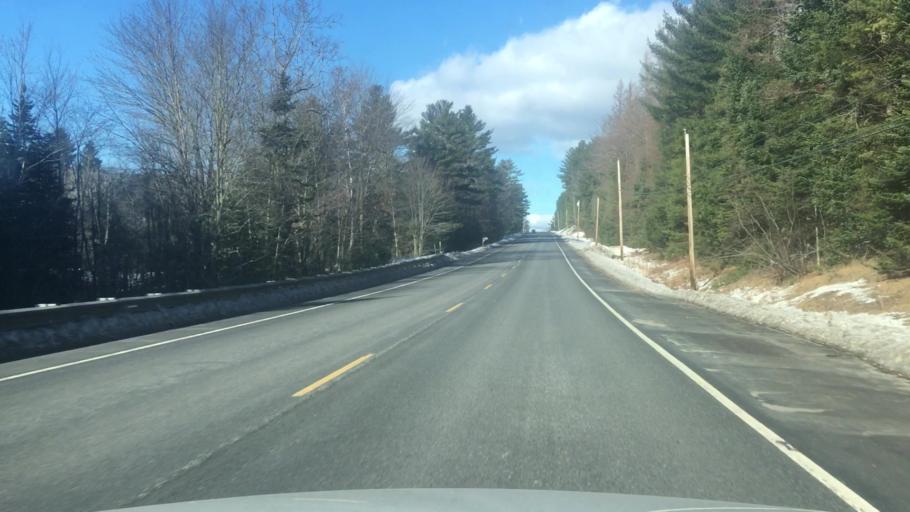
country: US
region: Maine
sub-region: Somerset County
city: Madison
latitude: 44.9298
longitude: -69.8336
